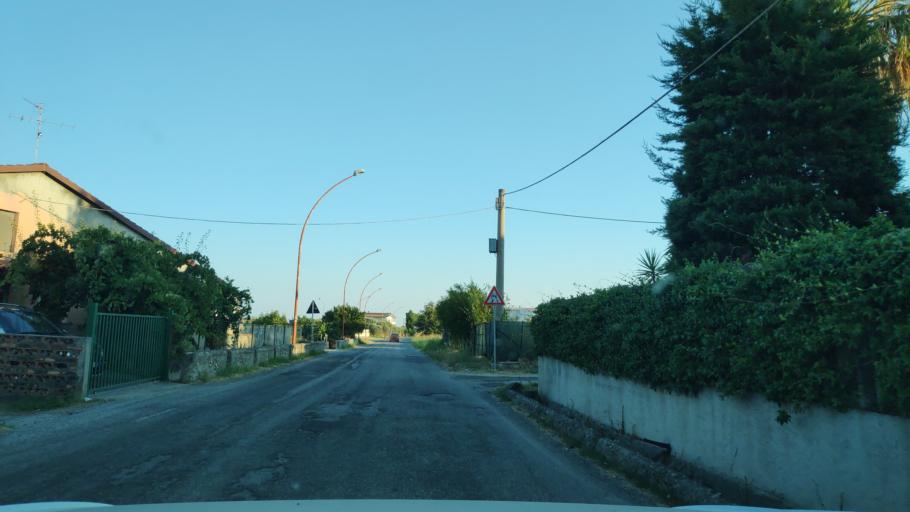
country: IT
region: Calabria
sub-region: Provincia di Reggio Calabria
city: Caulonia Marina
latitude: 38.3637
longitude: 16.4848
